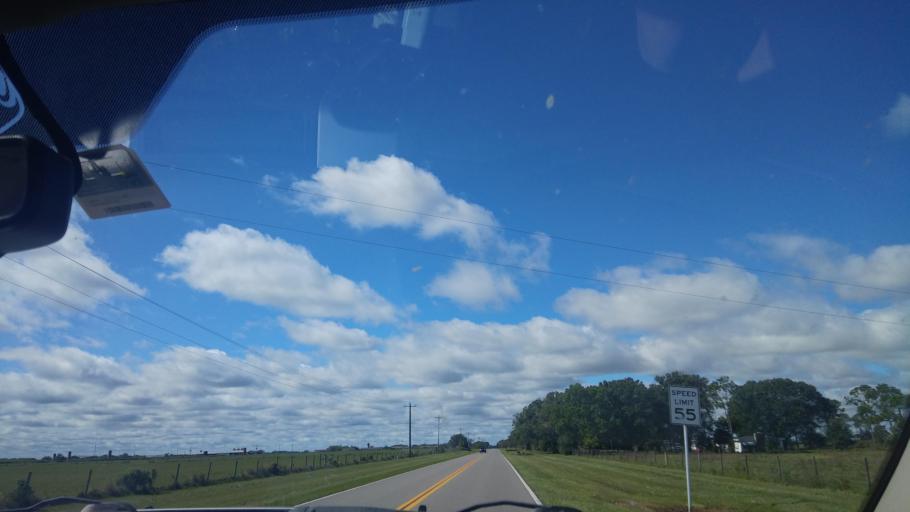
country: US
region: Florida
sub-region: Okeechobee County
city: Cypress Quarters
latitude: 27.3905
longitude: -80.8190
